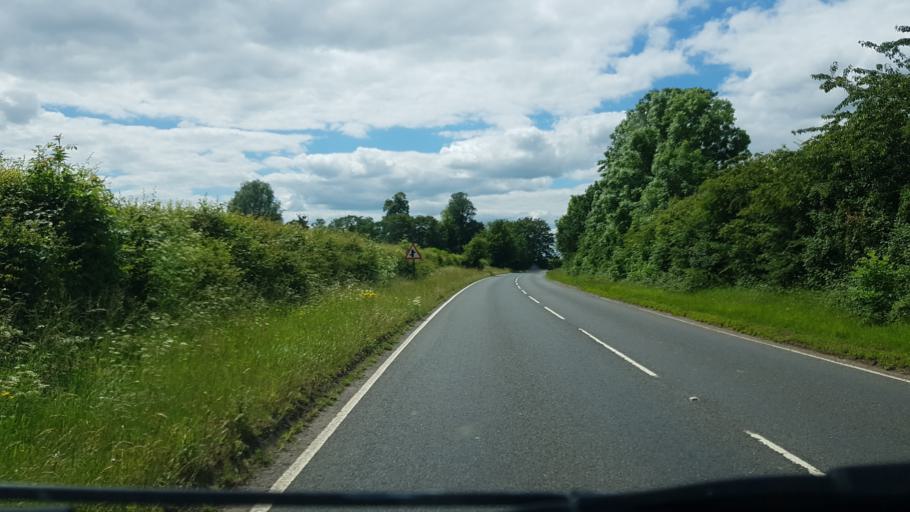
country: GB
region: England
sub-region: Worcestershire
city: Bromsgrove
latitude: 52.2601
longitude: -2.0686
